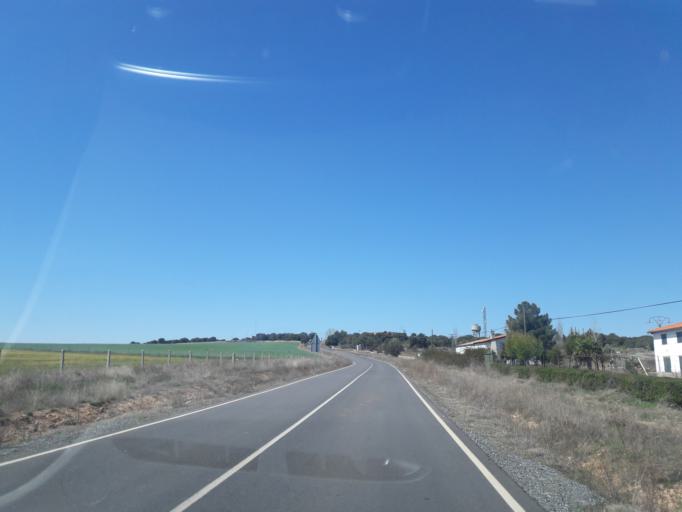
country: ES
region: Castille and Leon
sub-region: Provincia de Salamanca
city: Martinamor
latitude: 40.8106
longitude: -5.6241
